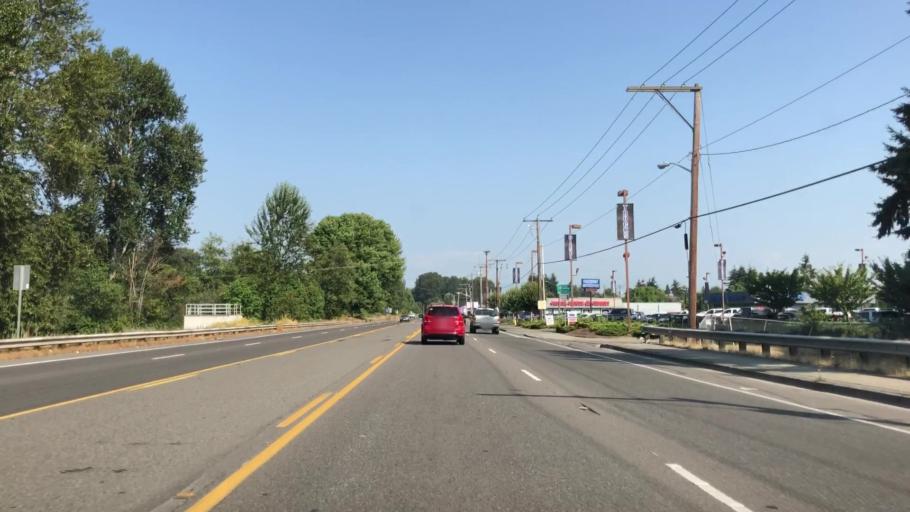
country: US
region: Washington
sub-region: Pierce County
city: Puyallup
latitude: 47.2068
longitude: -122.3220
